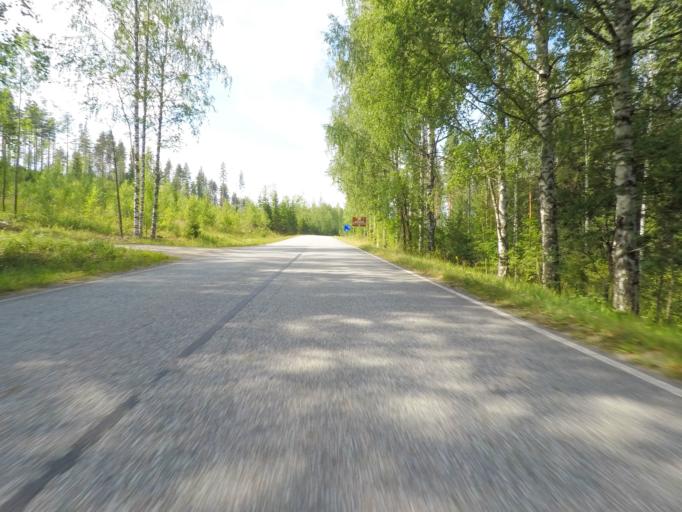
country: FI
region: Southern Savonia
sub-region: Savonlinna
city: Sulkava
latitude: 61.7195
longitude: 28.2076
